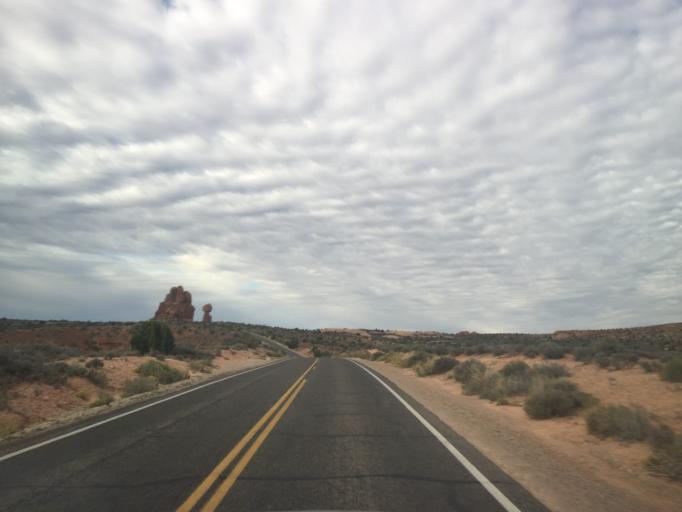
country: US
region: Utah
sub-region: Grand County
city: Moab
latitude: 38.7111
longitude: -109.5602
